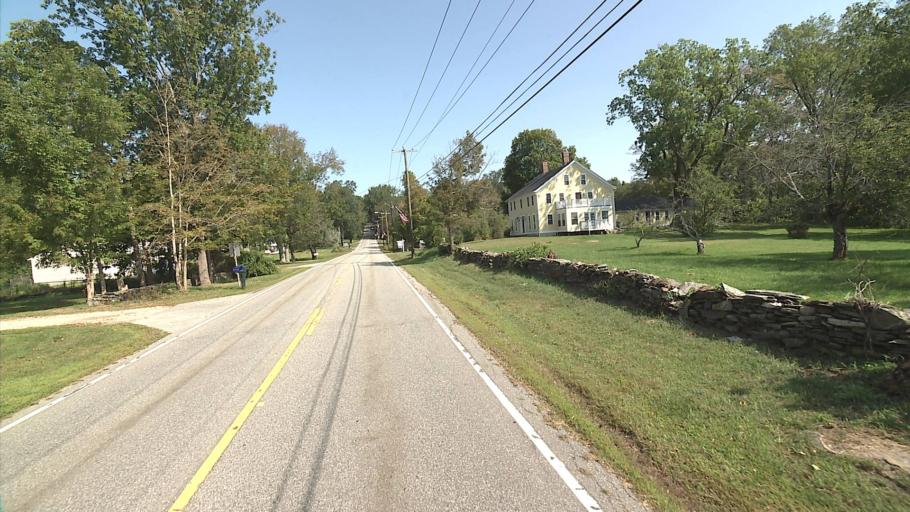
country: US
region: Connecticut
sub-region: Windham County
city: East Brooklyn
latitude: 41.7914
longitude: -71.9491
